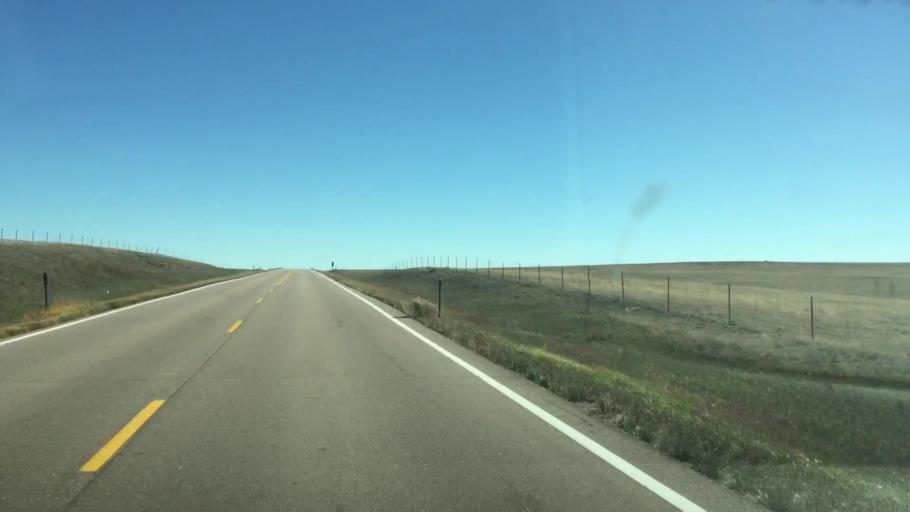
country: US
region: Colorado
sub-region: Lincoln County
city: Limon
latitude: 39.2753
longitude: -104.0044
